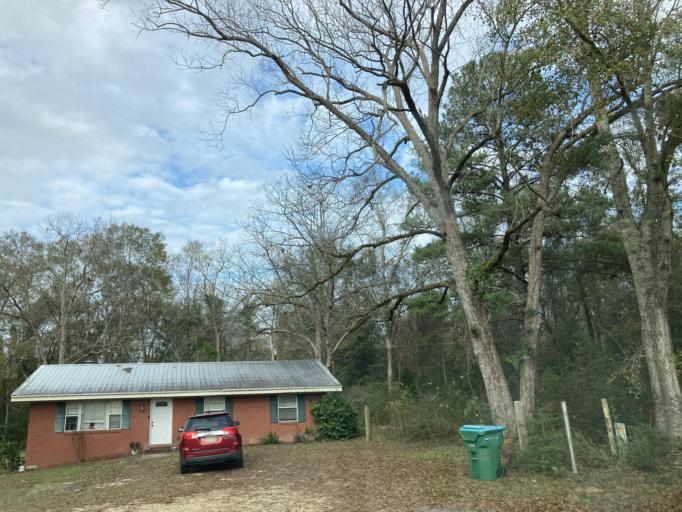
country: US
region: Mississippi
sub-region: Stone County
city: Wiggins
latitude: 30.9936
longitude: -89.2623
